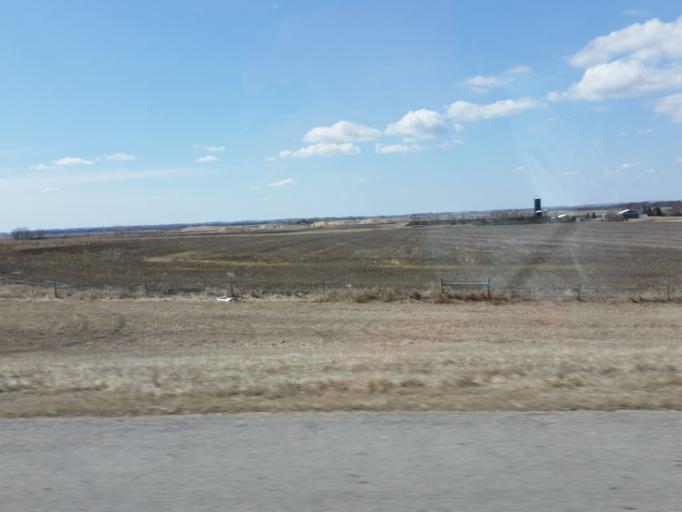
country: US
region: South Dakota
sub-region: Codington County
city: Watertown
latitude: 45.0353
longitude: -97.0549
